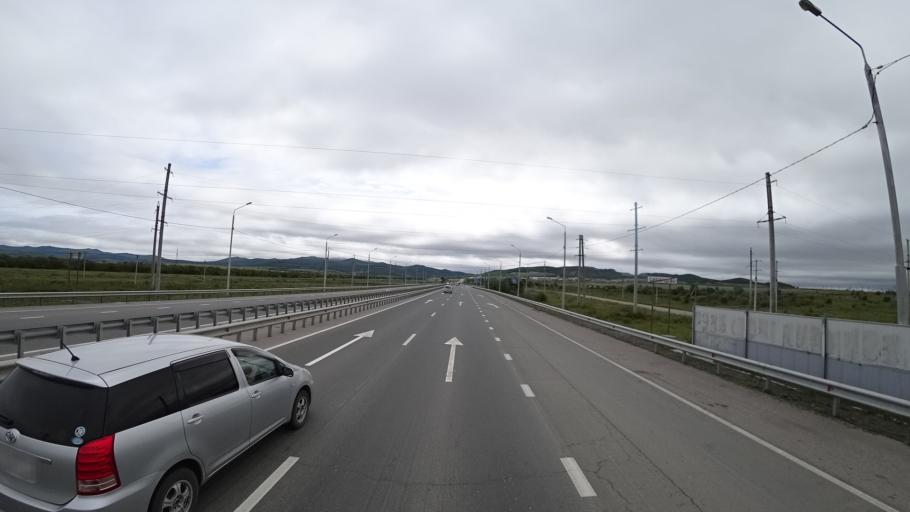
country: RU
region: Primorskiy
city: Monastyrishche
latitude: 44.1871
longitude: 132.4415
